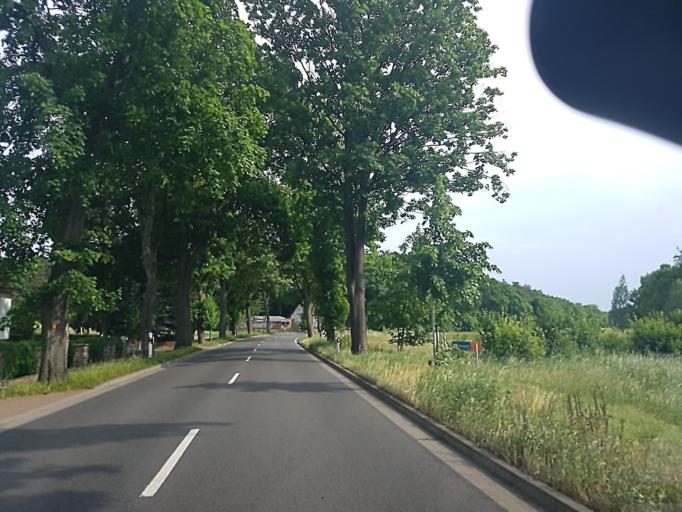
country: DE
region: Saxony-Anhalt
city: Nudersdorf
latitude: 51.9496
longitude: 12.6000
